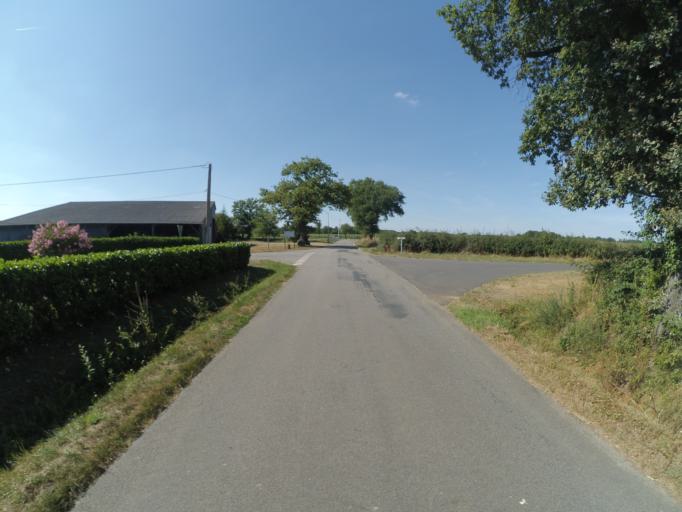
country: FR
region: Pays de la Loire
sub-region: Departement de la Loire-Atlantique
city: Vallet
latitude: 47.1925
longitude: -1.2663
